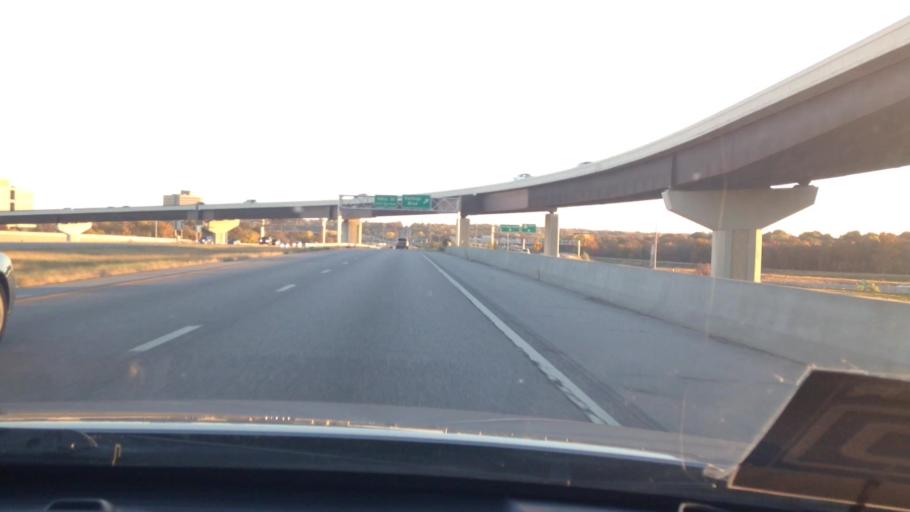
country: US
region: Kansas
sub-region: Johnson County
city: Lenexa
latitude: 38.9379
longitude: -94.7050
